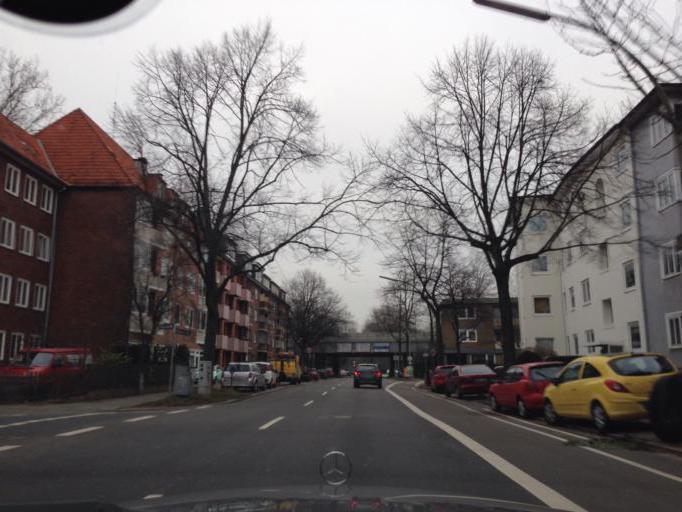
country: DE
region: Hamburg
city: Marienthal
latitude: 53.5734
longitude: 10.0560
